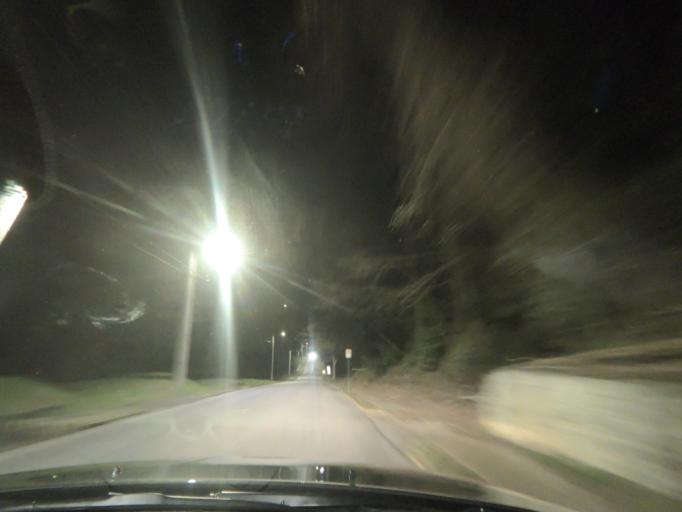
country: US
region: Georgia
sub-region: Fulton County
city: College Park
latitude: 33.6535
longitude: -84.4579
